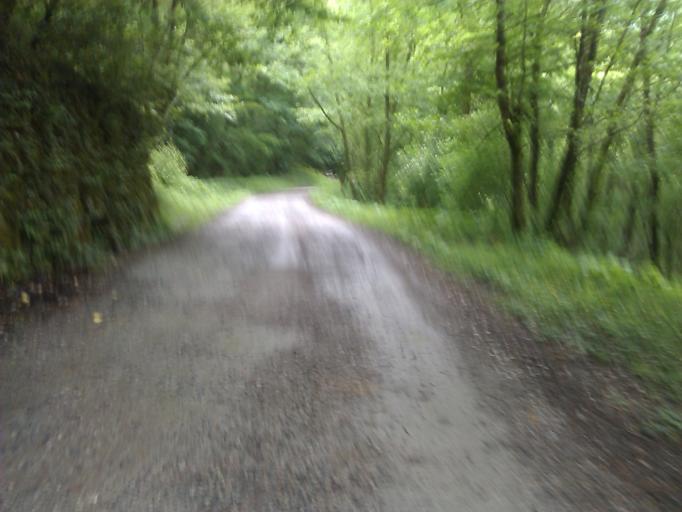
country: ES
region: Basque Country
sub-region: Provincia de Guipuzcoa
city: Andoain
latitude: 43.1866
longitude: -1.9953
